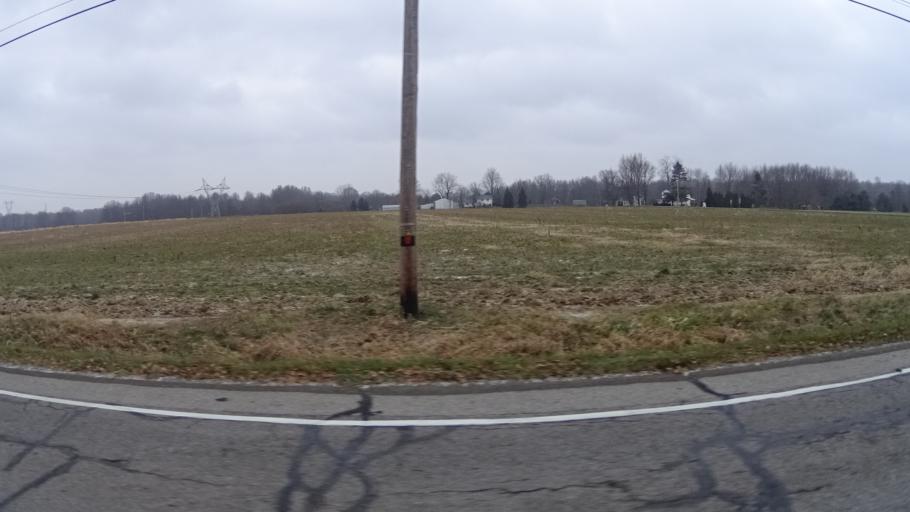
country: US
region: Ohio
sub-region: Lorain County
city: South Amherst
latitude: 41.3389
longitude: -82.2730
